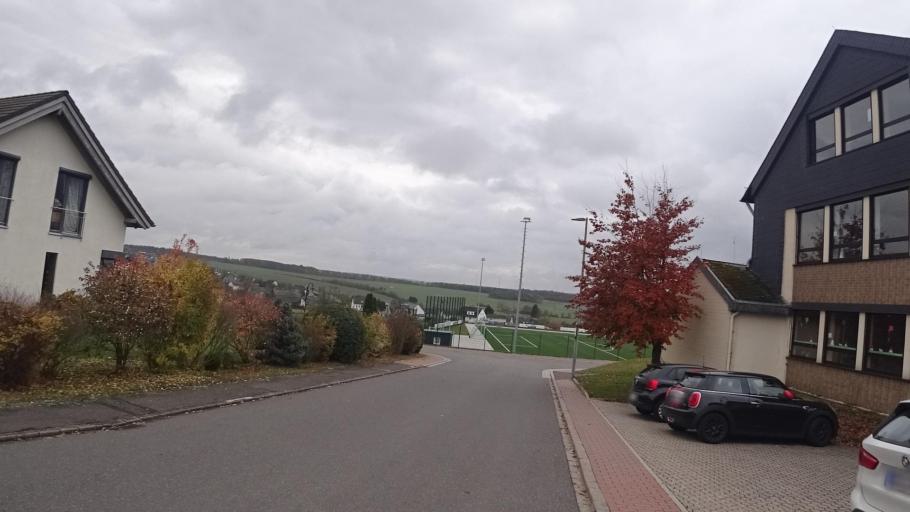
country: DE
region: Rheinland-Pfalz
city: Mermuth
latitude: 50.1617
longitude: 7.4898
